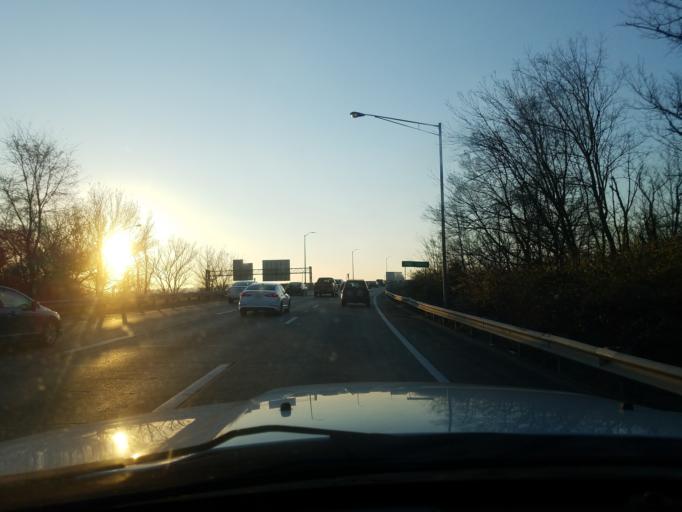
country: US
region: Indiana
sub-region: Floyd County
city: New Albany
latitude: 38.2752
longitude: -85.8142
